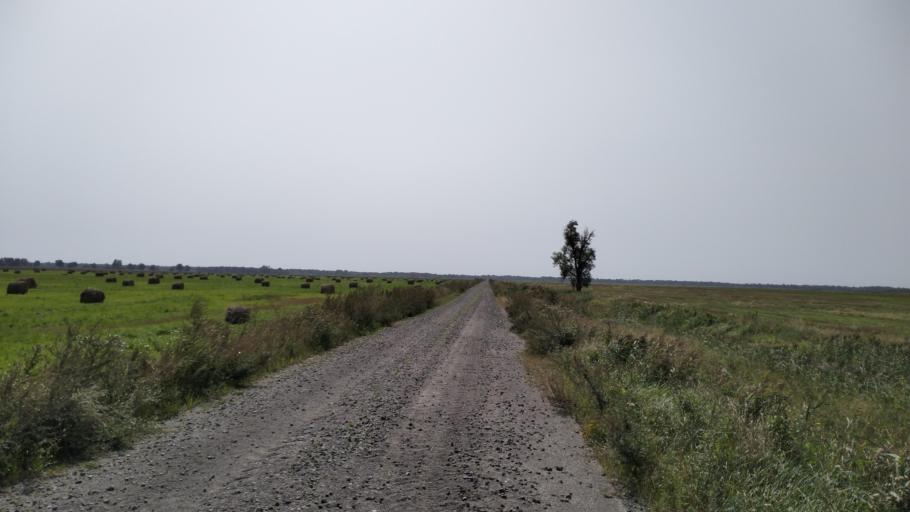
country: BY
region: Brest
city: Davyd-Haradok
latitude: 51.9945
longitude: 27.1763
